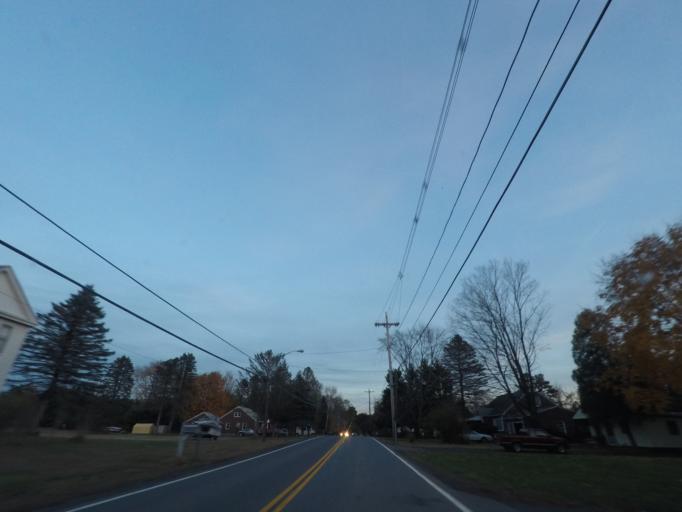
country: US
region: New York
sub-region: Schenectady County
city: Rotterdam
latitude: 42.7539
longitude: -73.9223
